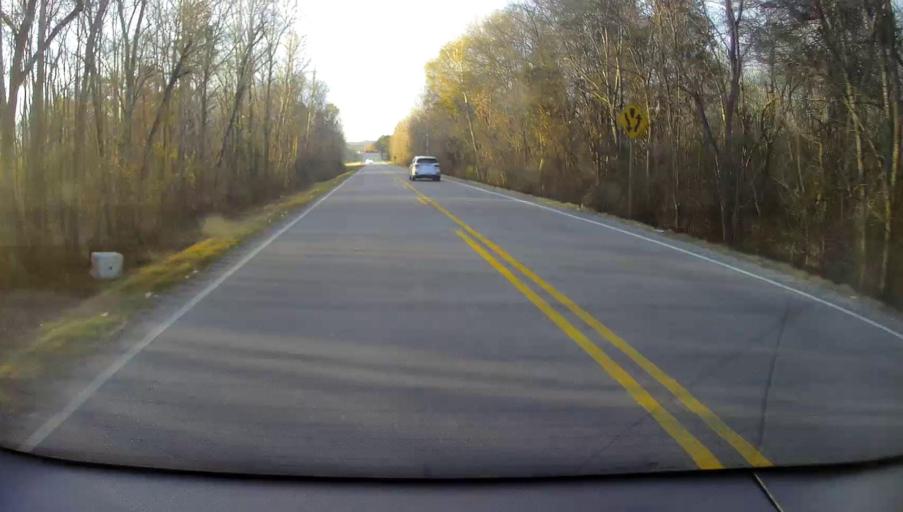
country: US
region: Alabama
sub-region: Blount County
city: Blountsville
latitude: 34.1567
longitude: -86.4626
